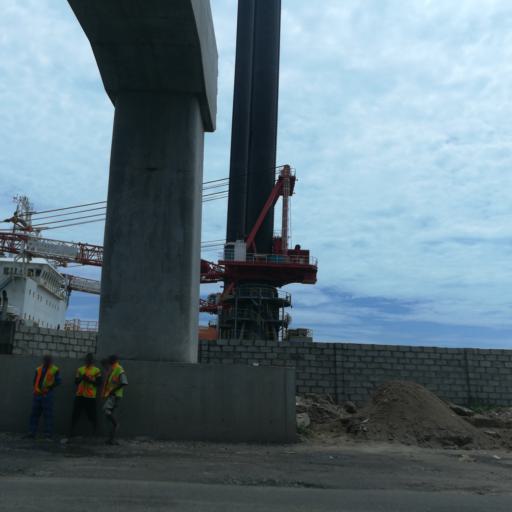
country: NG
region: Lagos
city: Lagos
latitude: 6.4529
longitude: 3.3839
